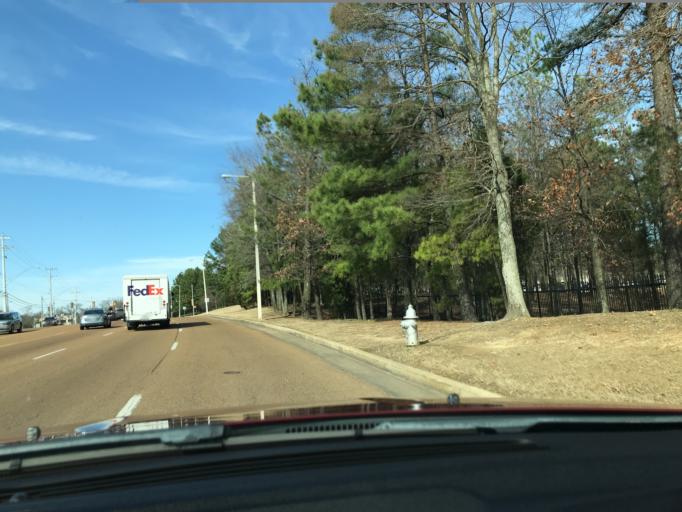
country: US
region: Tennessee
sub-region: Shelby County
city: Germantown
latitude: 35.0493
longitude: -89.7952
